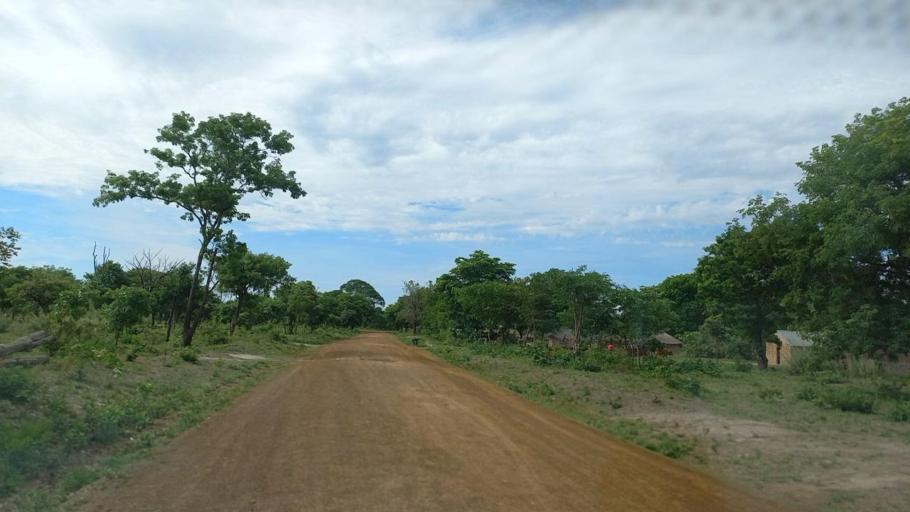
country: ZM
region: North-Western
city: Kabompo
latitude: -13.4580
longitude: 24.4271
